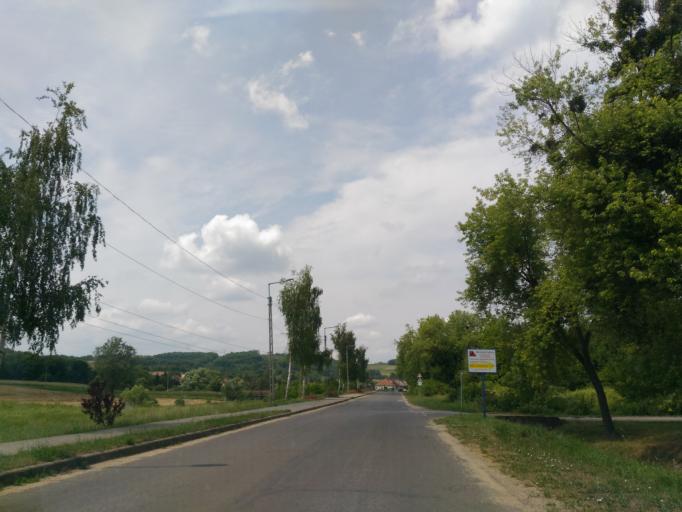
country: HU
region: Baranya
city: Komlo
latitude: 46.1916
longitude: 18.2342
